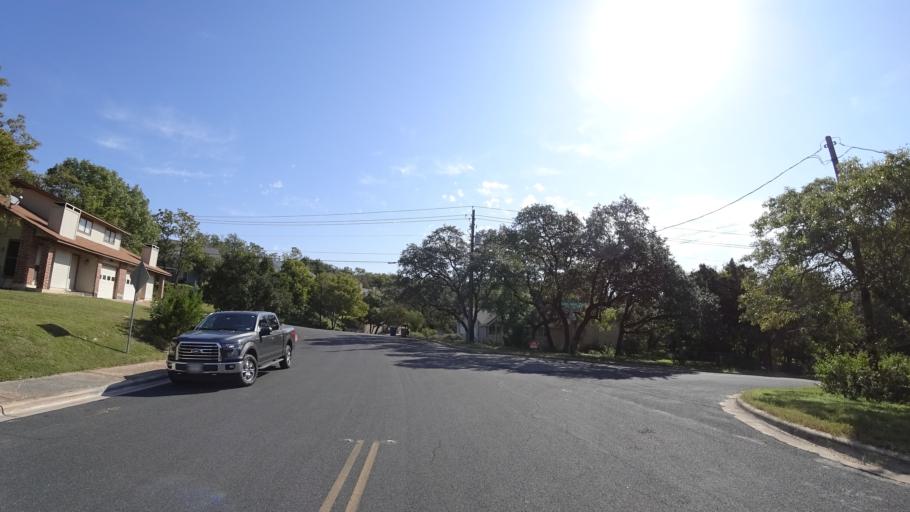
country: US
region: Texas
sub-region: Travis County
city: West Lake Hills
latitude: 30.3514
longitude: -97.7588
